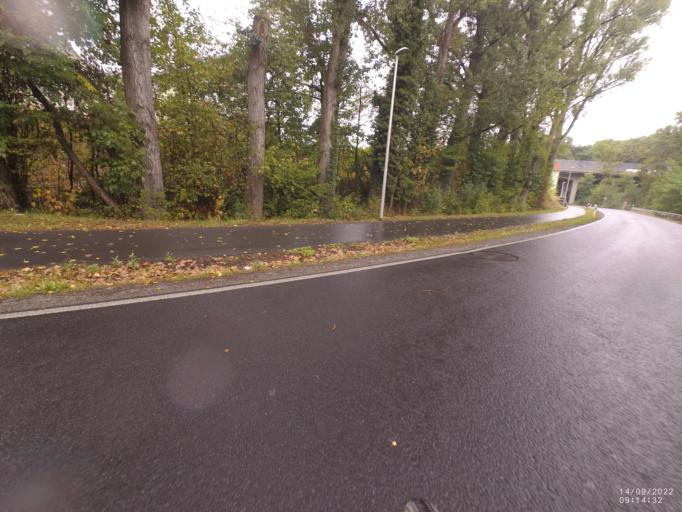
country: DE
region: Bavaria
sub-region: Regierungsbezirk Unterfranken
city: Glattbach
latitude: 49.9909
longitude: 9.1500
